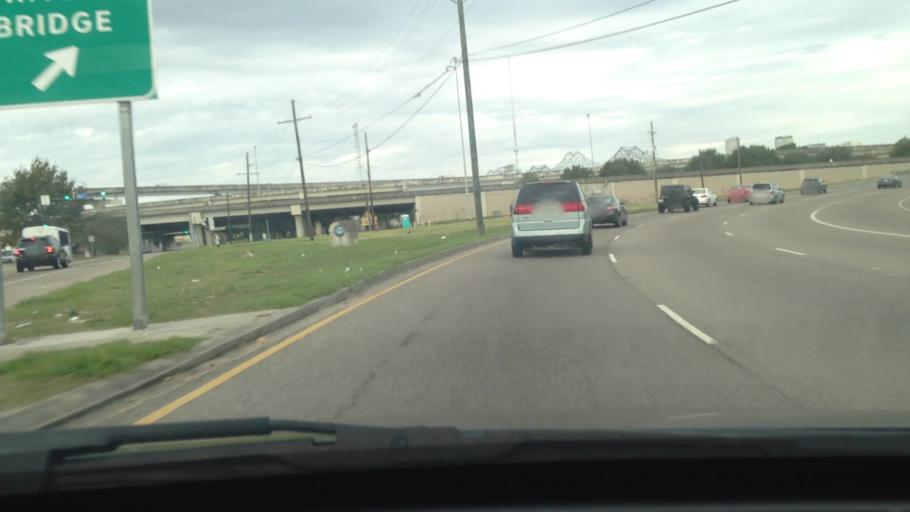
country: US
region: Louisiana
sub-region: Jefferson Parish
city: Terrytown
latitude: 29.9305
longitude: -90.0354
